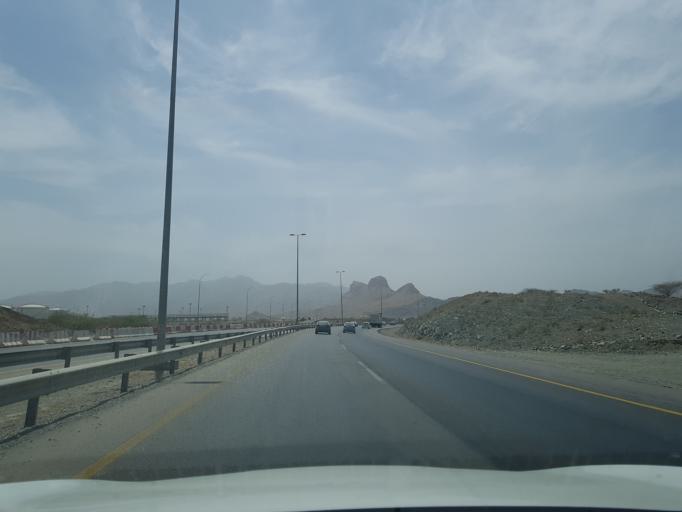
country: OM
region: Muhafazat ad Dakhiliyah
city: Bidbid
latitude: 23.5038
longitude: 58.1937
